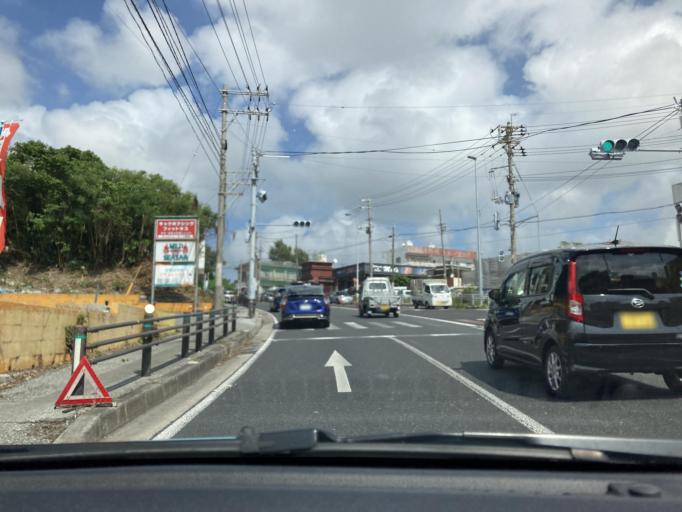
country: JP
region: Okinawa
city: Okinawa
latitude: 26.3306
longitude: 127.8224
